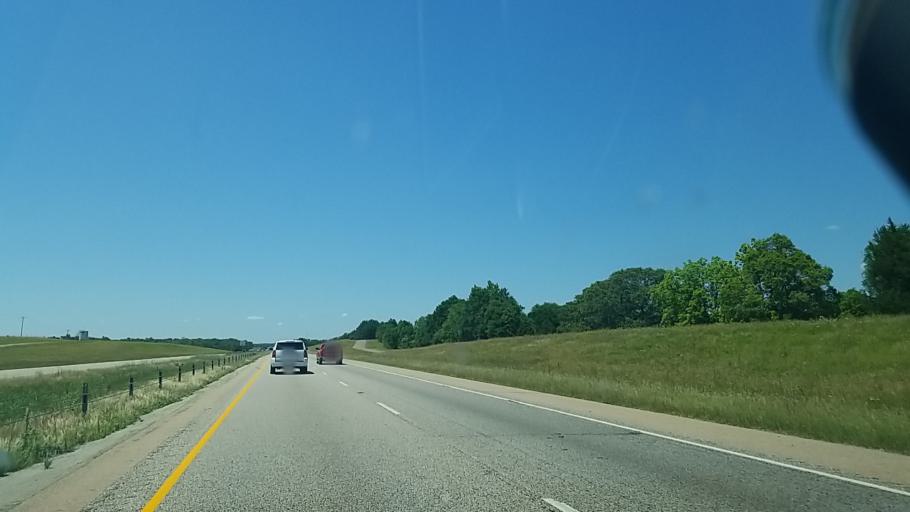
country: US
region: Texas
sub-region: Leon County
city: Buffalo
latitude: 31.3885
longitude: -96.0272
